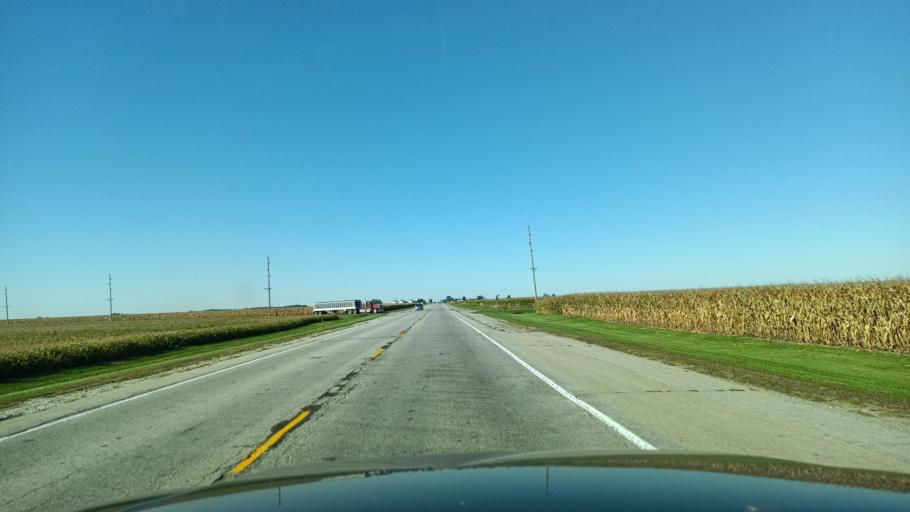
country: US
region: Illinois
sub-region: Warren County
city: Monmouth
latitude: 40.8883
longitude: -90.6700
